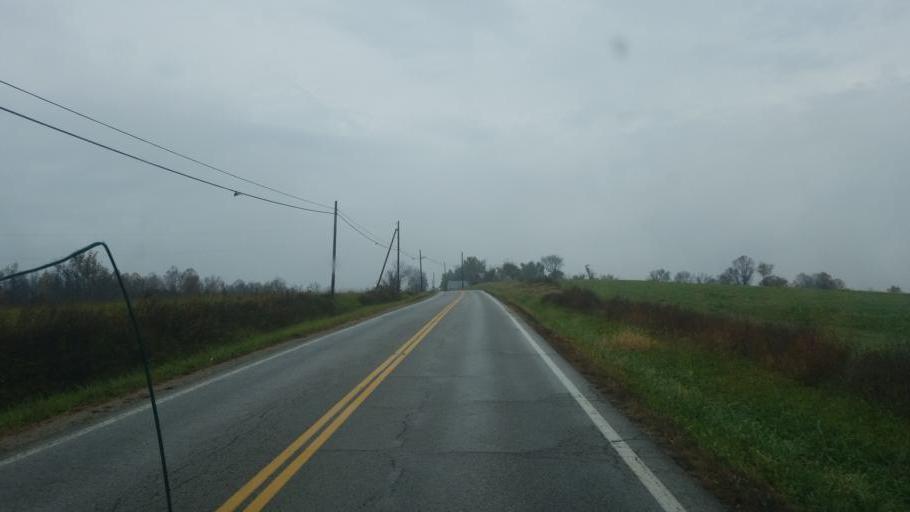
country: US
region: Ohio
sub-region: Morgan County
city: McConnelsville
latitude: 39.5107
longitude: -81.8533
